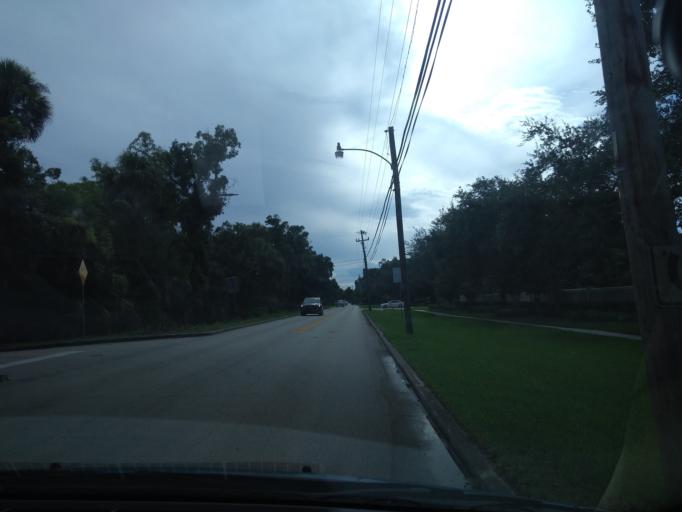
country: US
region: Florida
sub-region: Indian River County
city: Vero Beach South
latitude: 27.6314
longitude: -80.4361
